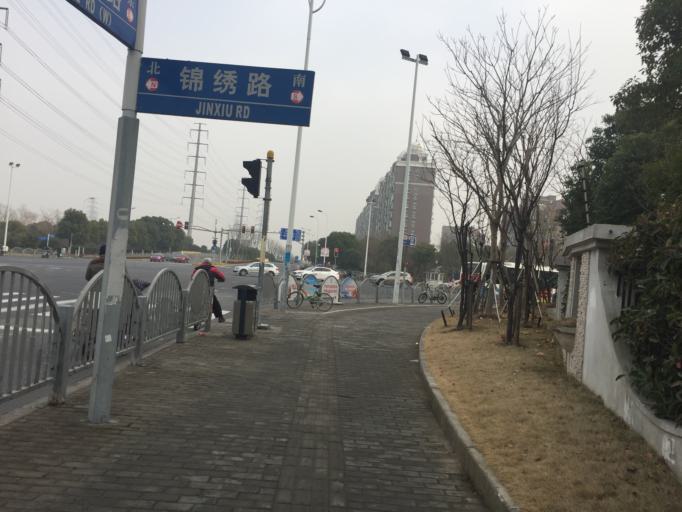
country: CN
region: Shanghai Shi
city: Huamu
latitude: 31.1895
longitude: 121.5353
